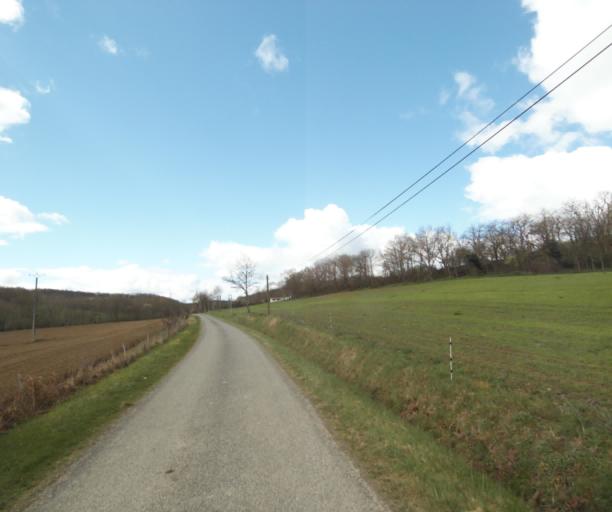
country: FR
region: Midi-Pyrenees
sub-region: Departement de l'Ariege
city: Saverdun
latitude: 43.1894
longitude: 1.5620
